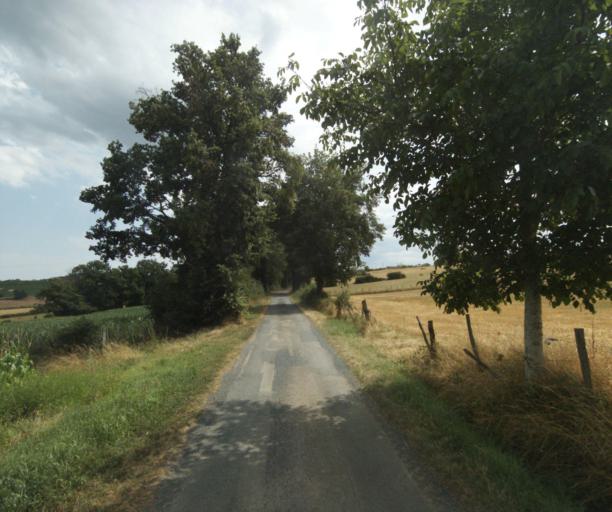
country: FR
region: Rhone-Alpes
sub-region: Departement du Rhone
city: Saint-Verand
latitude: 45.8915
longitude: 4.5519
